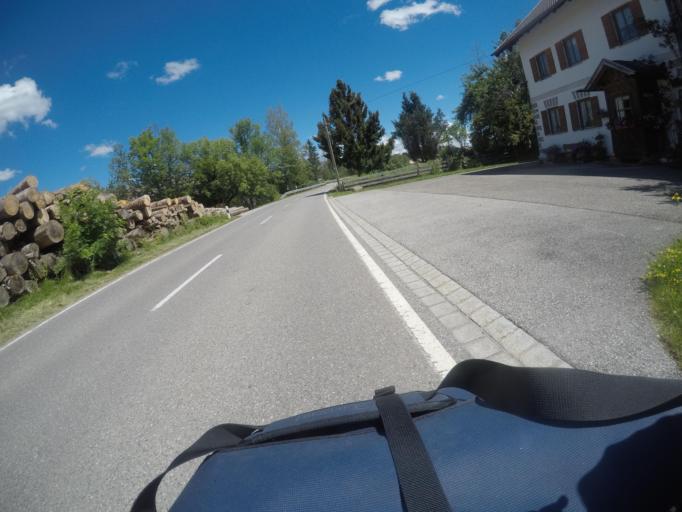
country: DE
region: Bavaria
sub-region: Upper Bavaria
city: Prem
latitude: 47.6717
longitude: 10.7897
